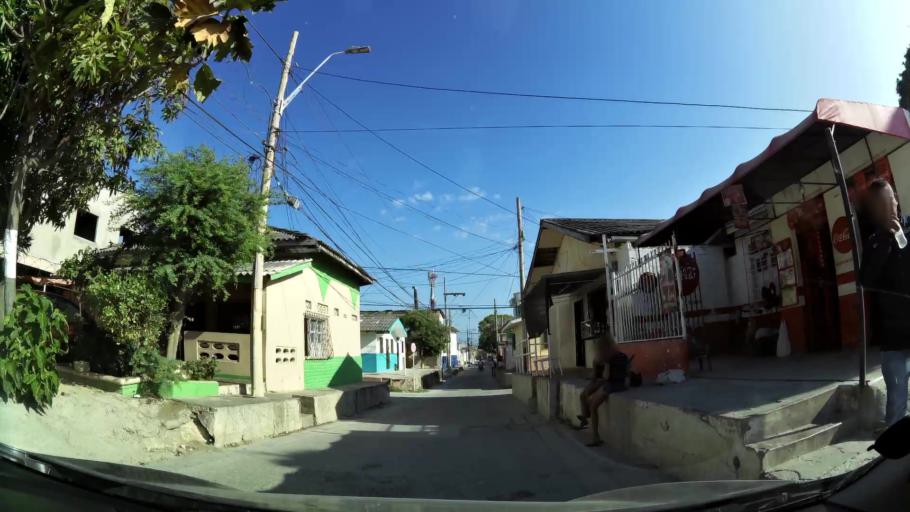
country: CO
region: Atlantico
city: Barranquilla
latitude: 10.9902
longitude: -74.7855
